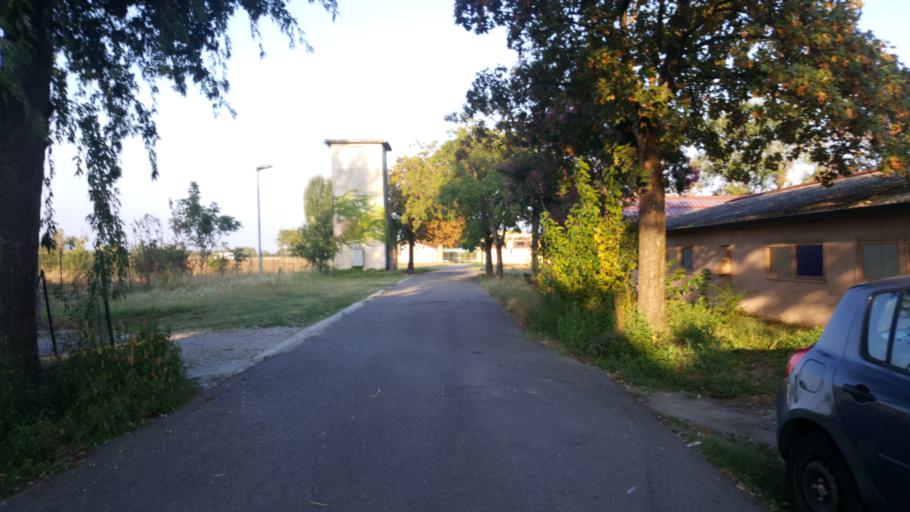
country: IT
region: Lombardy
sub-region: Provincia di Pavia
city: Rivanazzano
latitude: 44.9513
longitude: 9.0136
